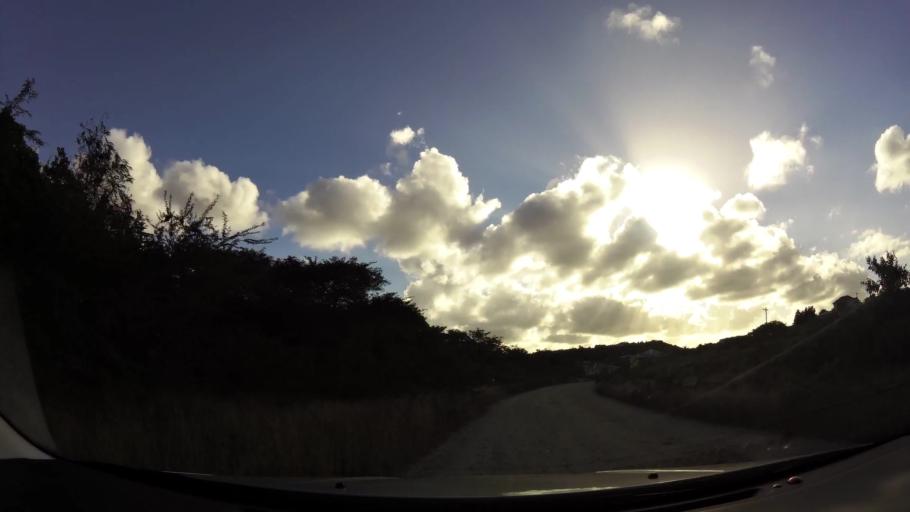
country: AG
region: Saint George
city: Piggotts
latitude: 17.1206
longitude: -61.7878
